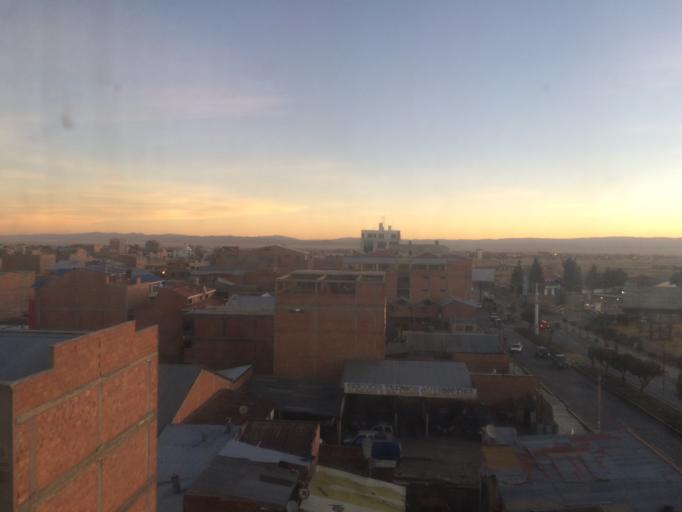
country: BO
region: La Paz
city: La Paz
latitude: -16.5088
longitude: -68.1665
